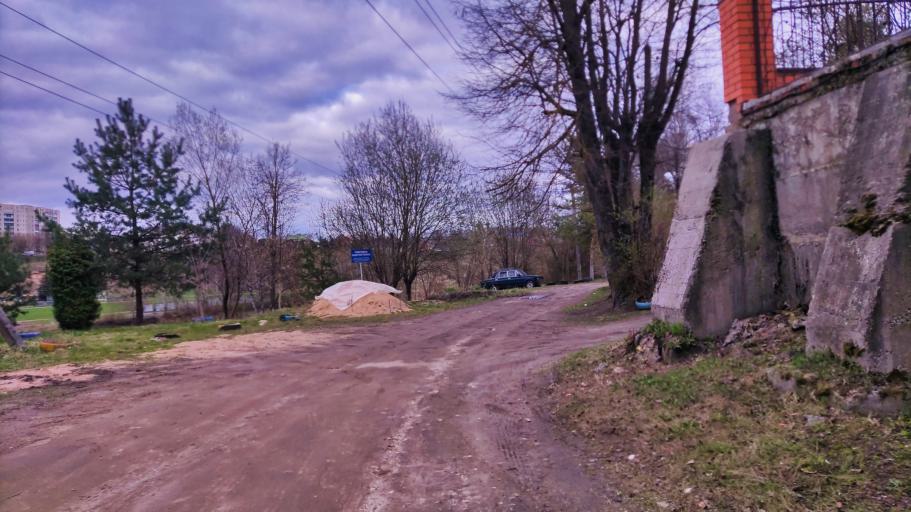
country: RU
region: Tverskaya
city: Rzhev
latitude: 56.2548
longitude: 34.3377
